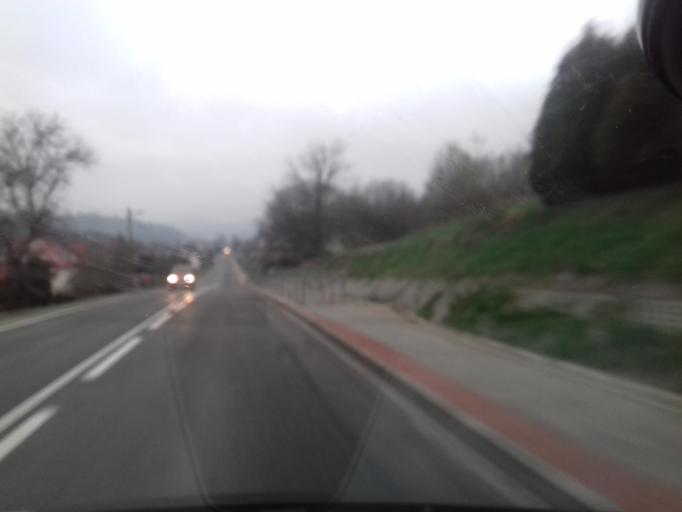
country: PL
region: Lesser Poland Voivodeship
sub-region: Powiat limanowski
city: Mszana Gorna
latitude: 49.6877
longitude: 20.1133
